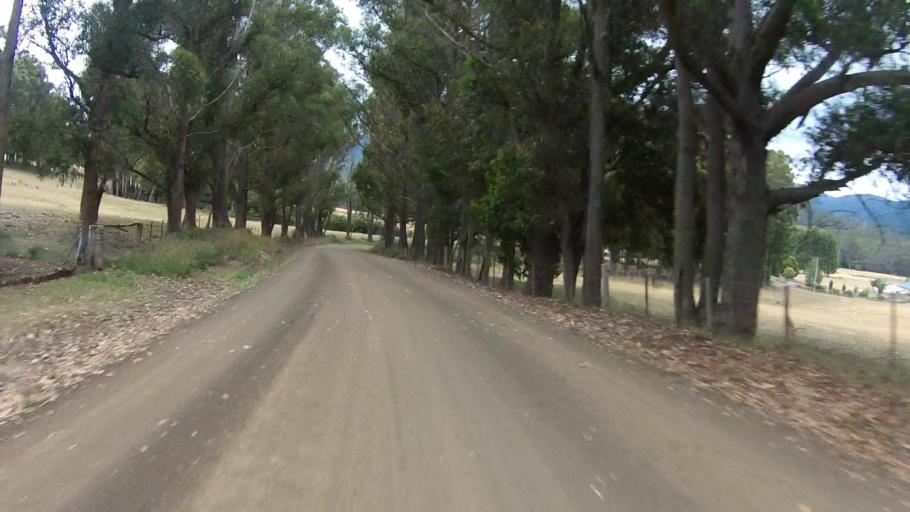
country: AU
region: Tasmania
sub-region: Huon Valley
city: Huonville
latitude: -42.9640
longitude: 147.0770
